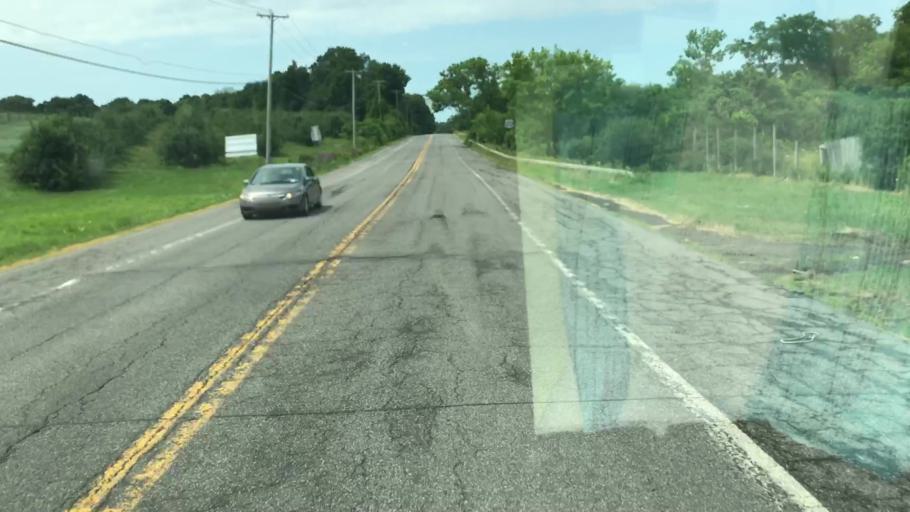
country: US
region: New York
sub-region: Onondaga County
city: Nedrow
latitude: 42.9107
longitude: -76.2221
